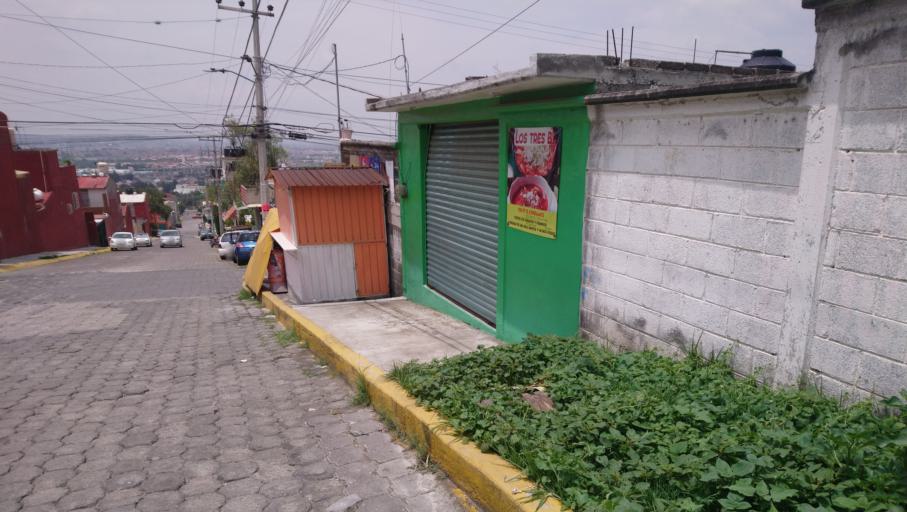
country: MX
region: Mexico
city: Coacalco
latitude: 19.6244
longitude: -99.1140
